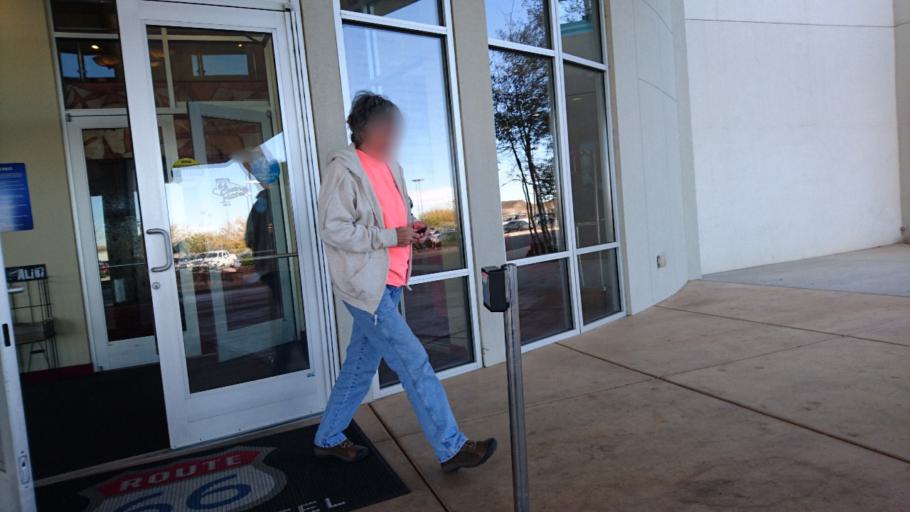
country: US
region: New Mexico
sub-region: Bernalillo County
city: South Valley
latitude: 35.0288
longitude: -106.9531
